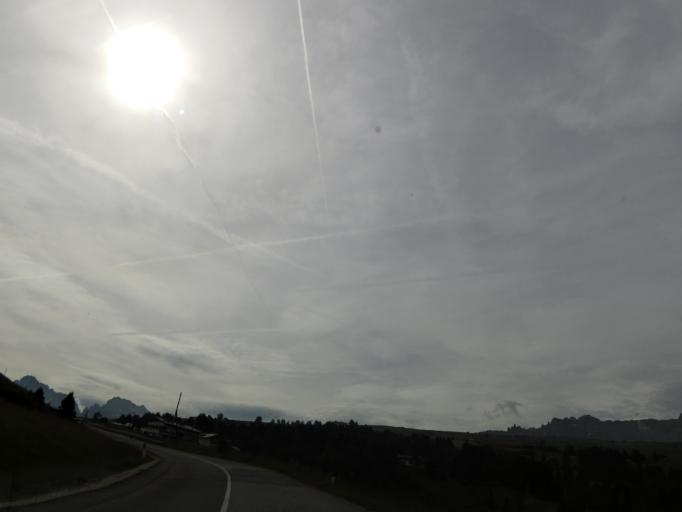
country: IT
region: Trentino-Alto Adige
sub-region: Bolzano
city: Siusi
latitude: 46.5408
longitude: 11.6116
